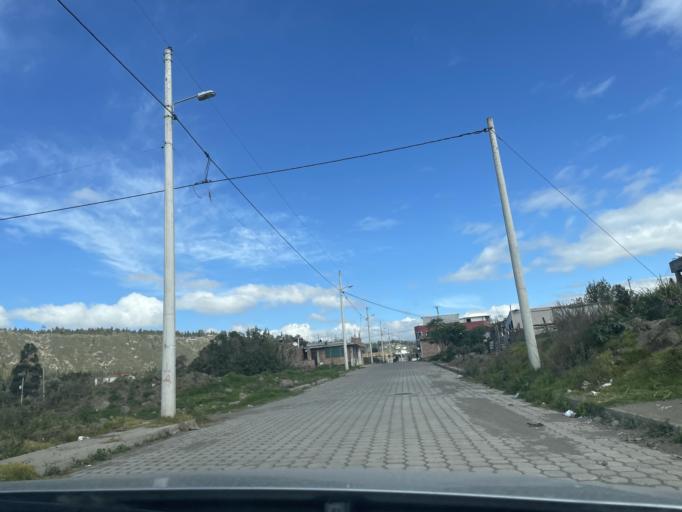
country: EC
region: Chimborazo
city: Guano
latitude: -1.6063
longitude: -78.6294
